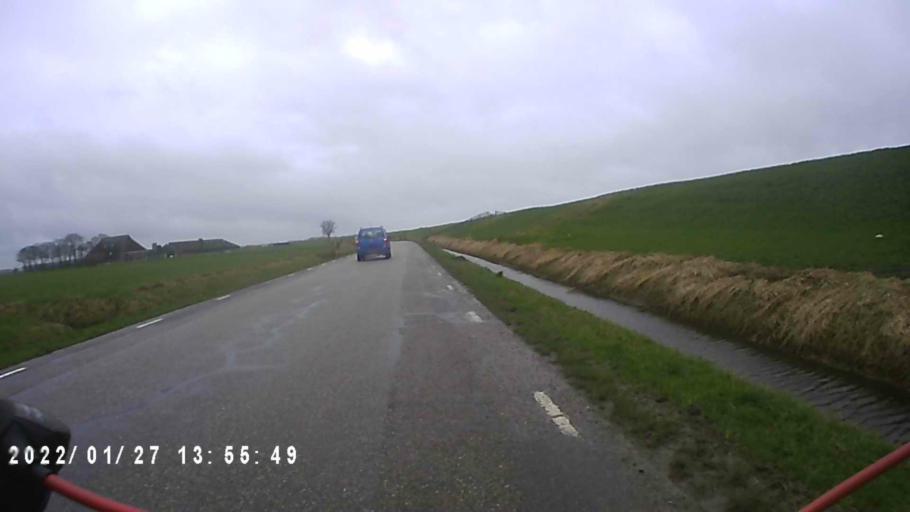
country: NL
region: Friesland
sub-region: Gemeente Kollumerland en Nieuwkruisland
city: Kollum
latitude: 53.3073
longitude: 6.1835
